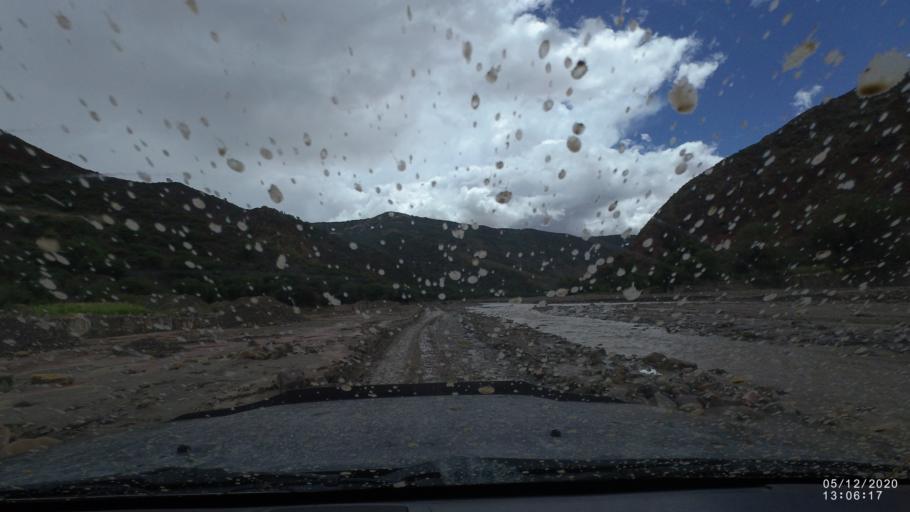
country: BO
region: Cochabamba
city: Sipe Sipe
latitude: -17.5575
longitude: -66.4442
